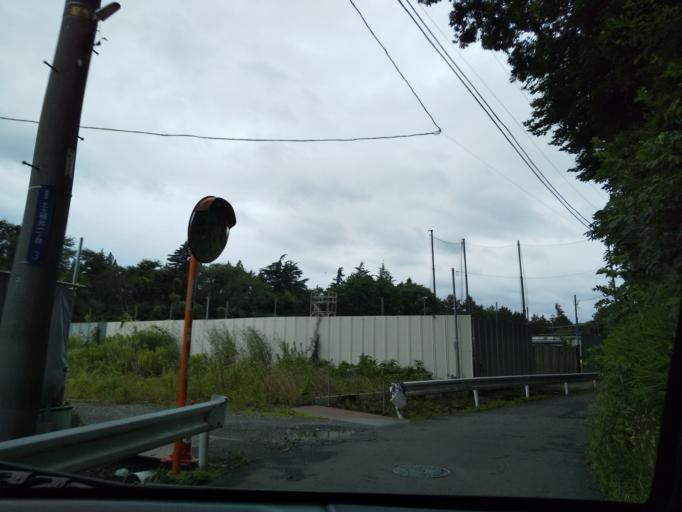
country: JP
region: Kanagawa
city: Minami-rinkan
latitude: 35.4244
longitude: 139.4429
